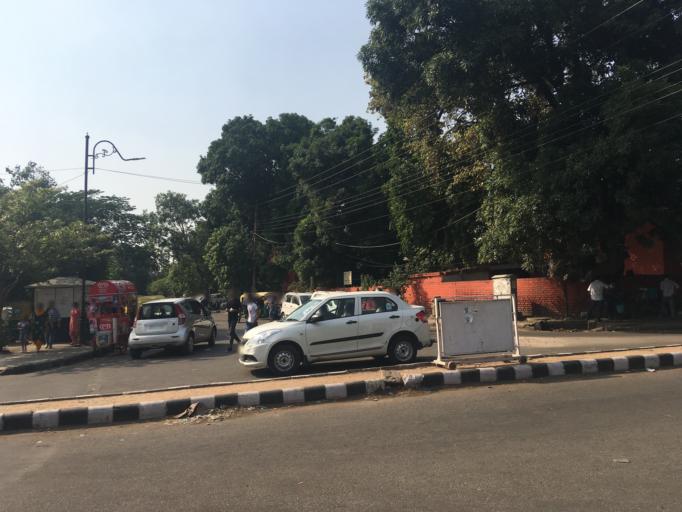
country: IN
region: Chandigarh
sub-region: Chandigarh
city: Chandigarh
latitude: 30.7067
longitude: 76.8011
